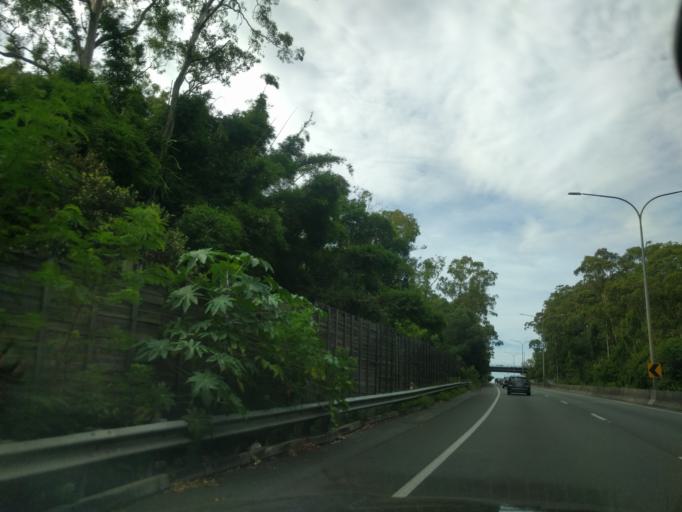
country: AU
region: Queensland
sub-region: Brisbane
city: Kenmore Hills
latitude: -27.5215
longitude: 152.9483
